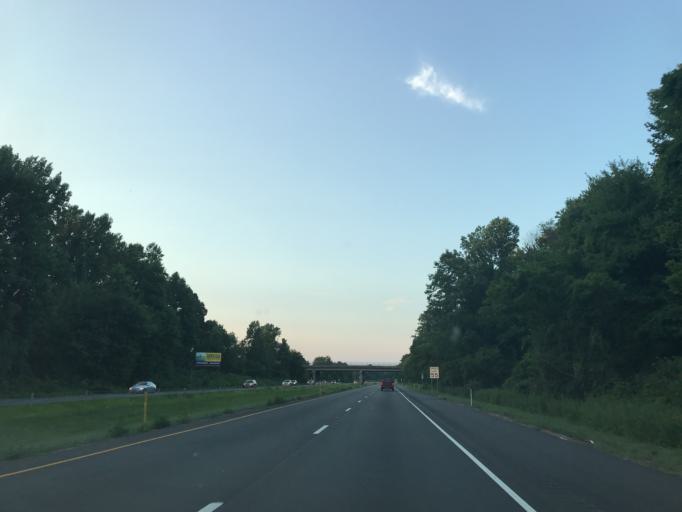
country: US
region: Pennsylvania
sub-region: Bucks County
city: Woodbourne
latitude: 40.1738
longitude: -74.8974
